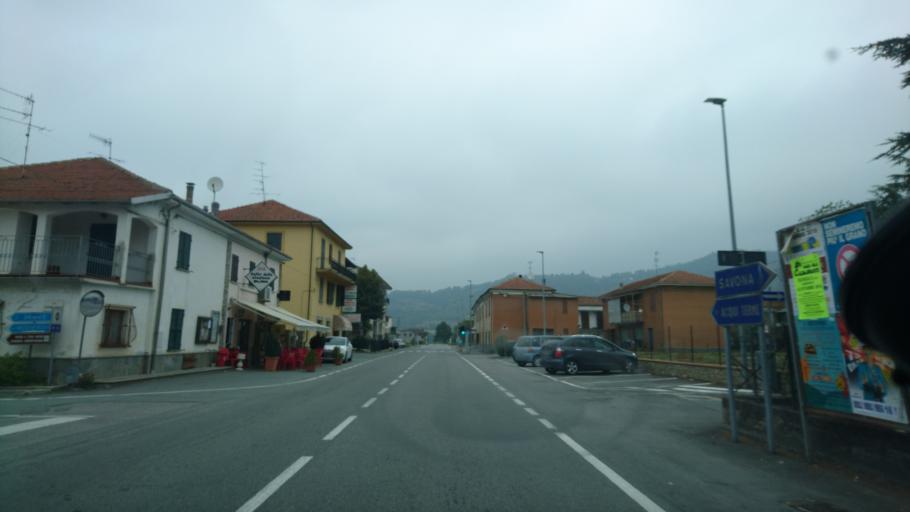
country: IT
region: Piedmont
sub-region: Provincia di Alessandria
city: Denice
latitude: 44.6006
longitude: 8.3534
